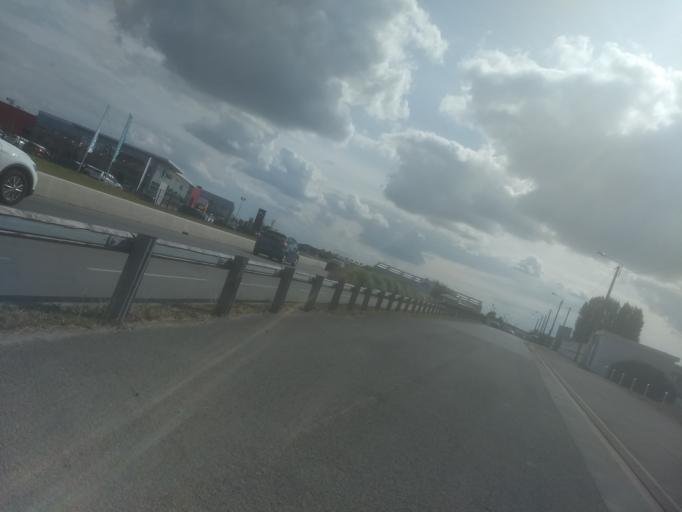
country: FR
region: Nord-Pas-de-Calais
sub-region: Departement du Pas-de-Calais
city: Beaurains
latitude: 50.2678
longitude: 2.7979
